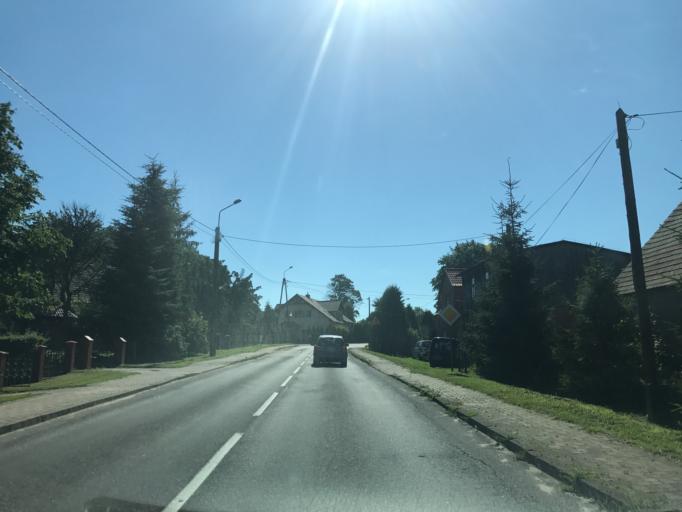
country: PL
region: Pomeranian Voivodeship
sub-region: Powiat bytowski
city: Czarna Dabrowka
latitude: 54.3558
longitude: 17.5671
